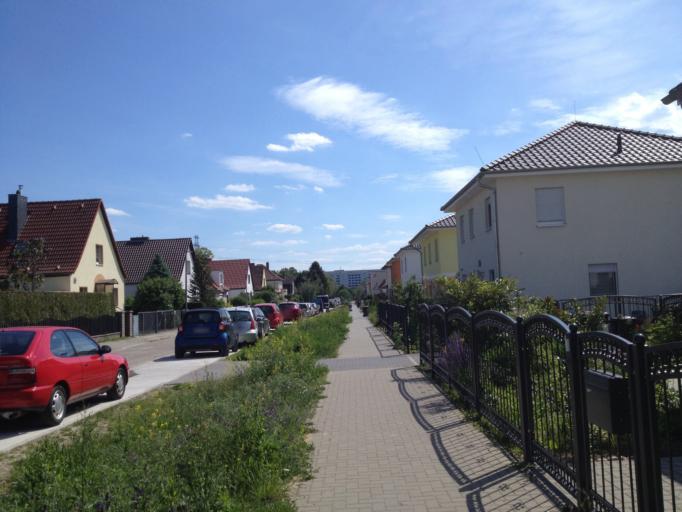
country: DE
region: Berlin
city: Friedrichsfelde
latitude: 52.5195
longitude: 13.5276
